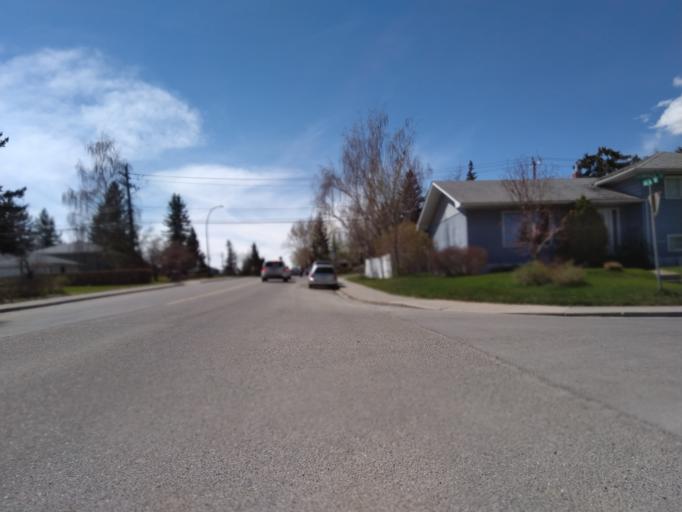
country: CA
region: Alberta
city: Calgary
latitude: 51.0126
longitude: -114.1514
